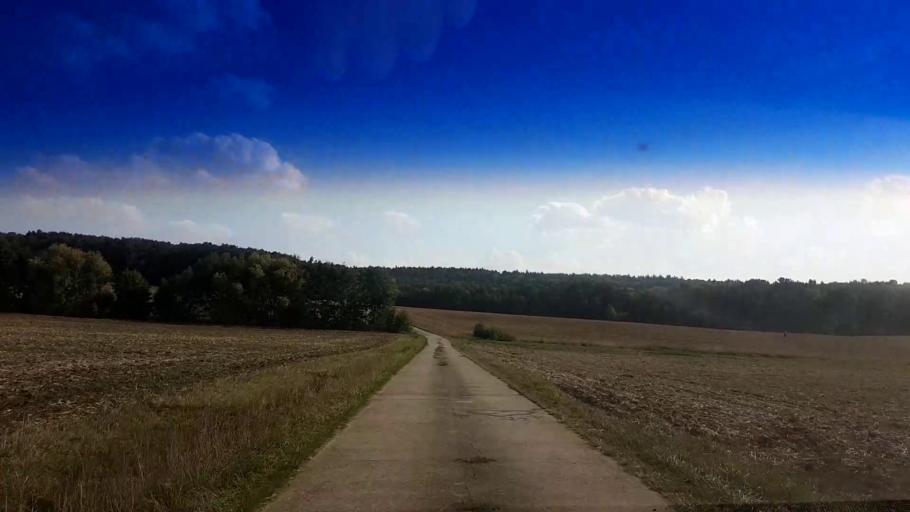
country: DE
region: Bavaria
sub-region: Upper Franconia
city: Litzendorf
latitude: 49.9392
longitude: 10.9995
